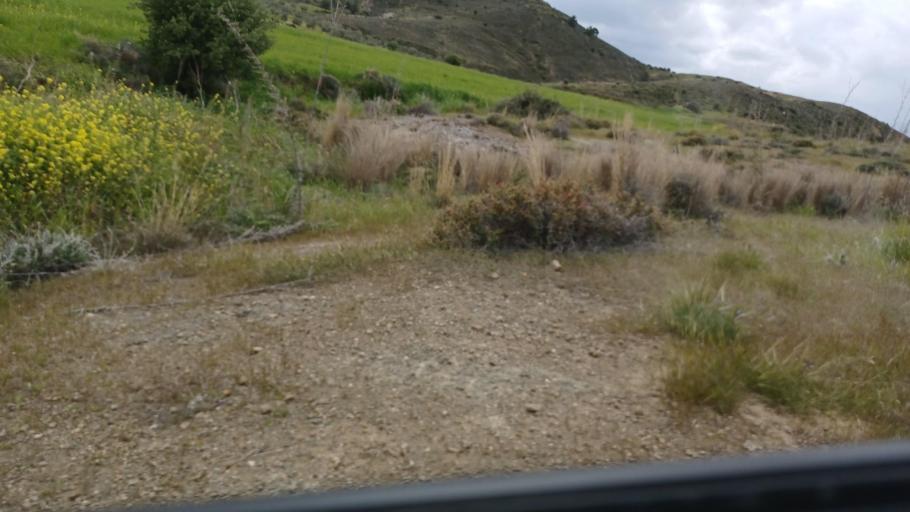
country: CY
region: Lefkosia
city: Lefka
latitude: 35.0888
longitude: 32.9406
